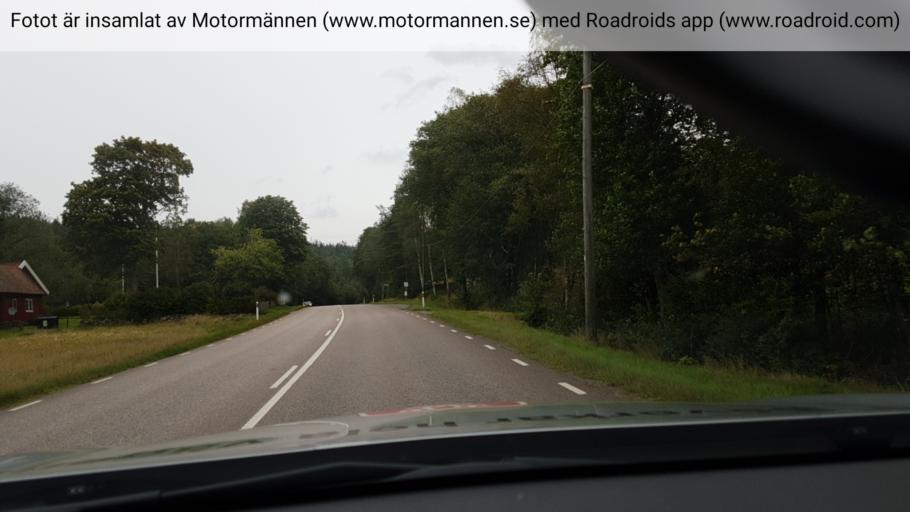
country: SE
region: Vaestra Goetaland
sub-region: Harryda Kommun
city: Landvetter
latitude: 57.6031
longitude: 12.2108
